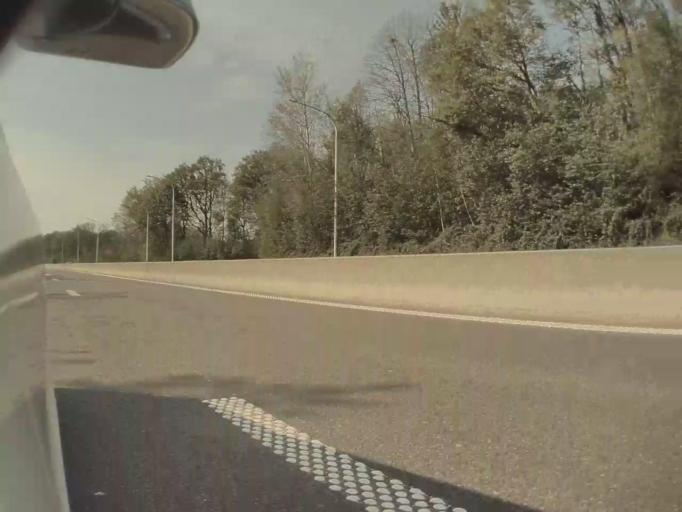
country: BE
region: Wallonia
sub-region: Province de Namur
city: Hamois
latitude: 50.3084
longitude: 5.1540
